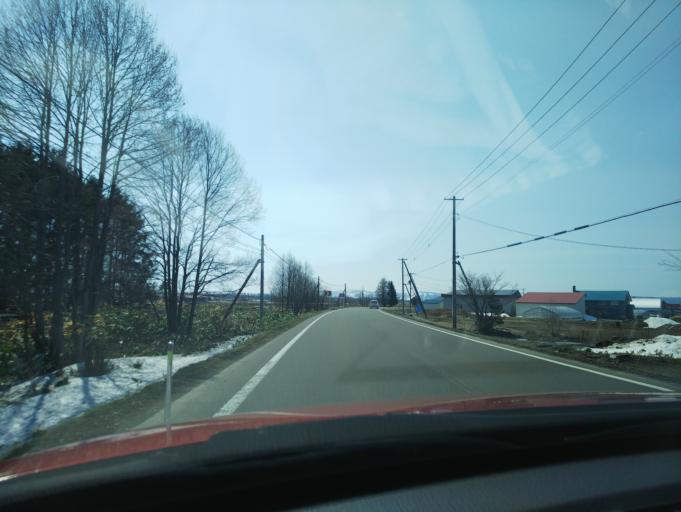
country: JP
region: Hokkaido
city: Nayoro
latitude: 44.3169
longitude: 142.4629
